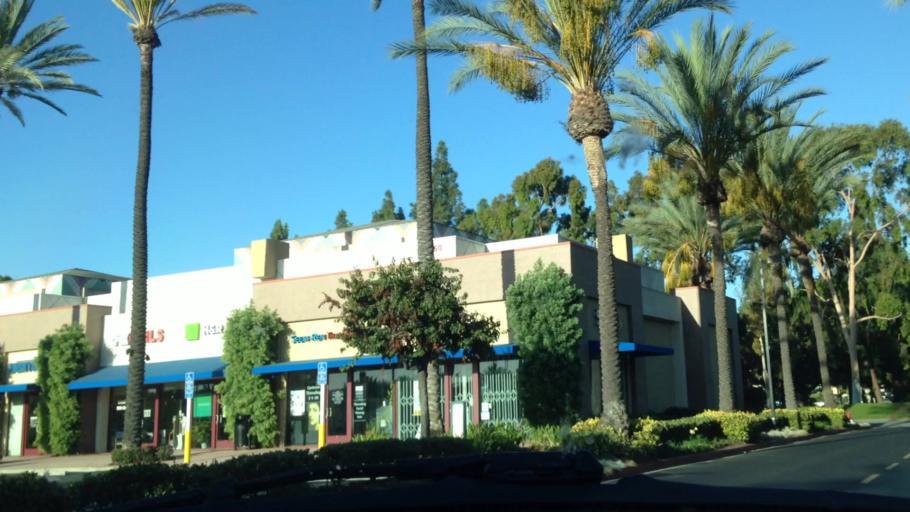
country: US
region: California
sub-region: Los Angeles County
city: Cerritos
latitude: 33.8720
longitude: -118.0630
